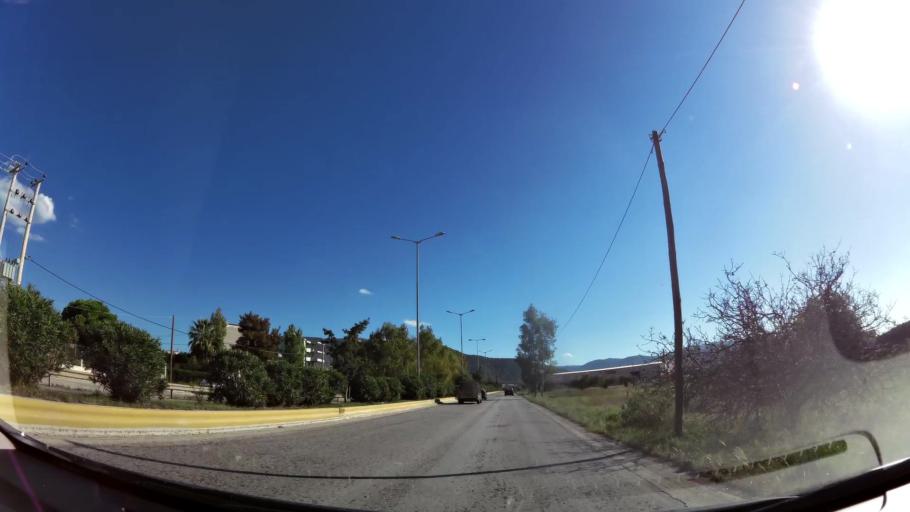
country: GR
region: Attica
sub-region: Nomarchia Anatolikis Attikis
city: Markopoulo
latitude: 37.8781
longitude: 23.9286
